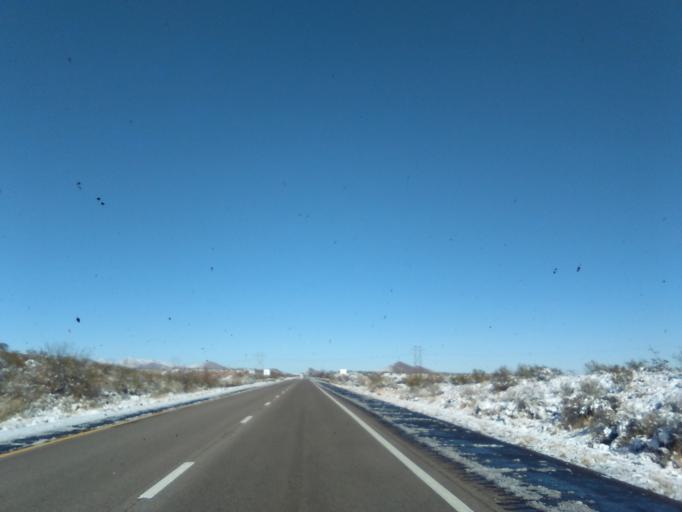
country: US
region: New Mexico
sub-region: Socorro County
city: Socorro
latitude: 33.7137
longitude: -107.0358
